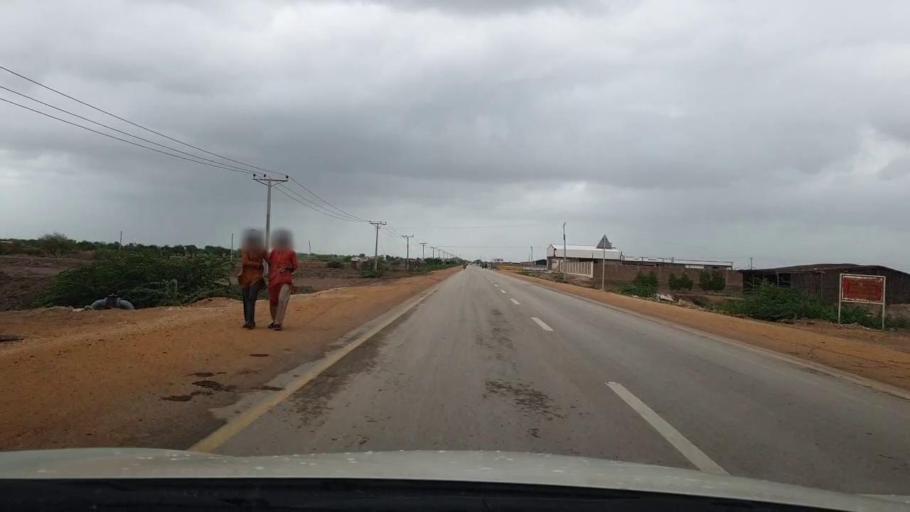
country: PK
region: Sindh
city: Badin
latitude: 24.6539
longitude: 68.7647
